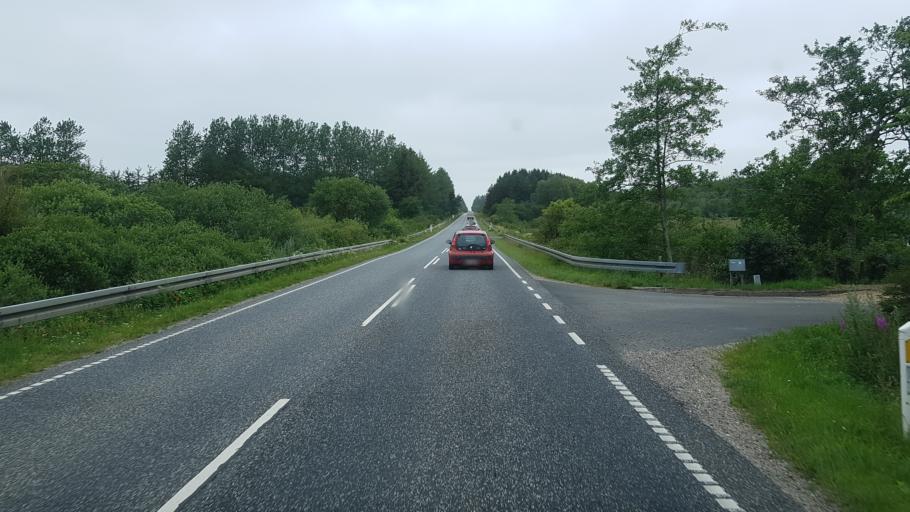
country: DK
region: Central Jutland
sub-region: Lemvig Kommune
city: Lemvig
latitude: 56.4576
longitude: 8.3360
